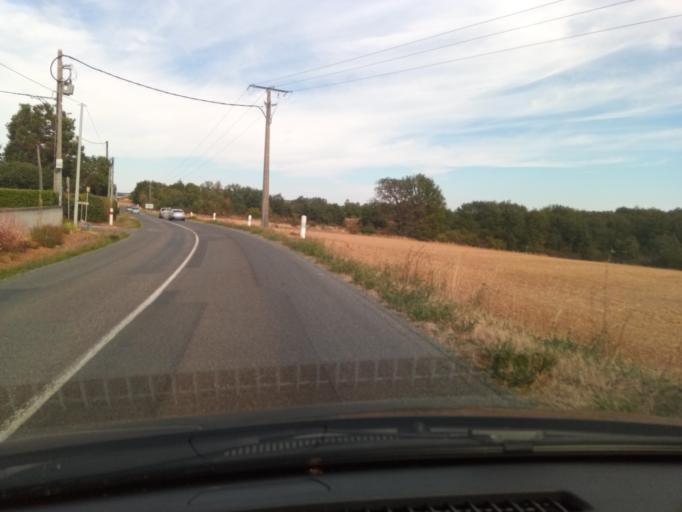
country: FR
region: Poitou-Charentes
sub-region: Departement de la Vienne
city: Chauvigny
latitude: 46.5586
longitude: 0.6161
